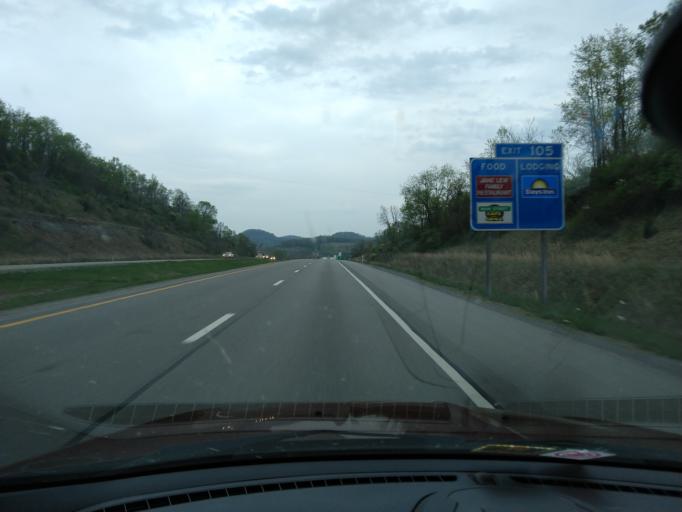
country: US
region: West Virginia
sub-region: Lewis County
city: Weston
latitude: 39.0840
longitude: -80.3985
